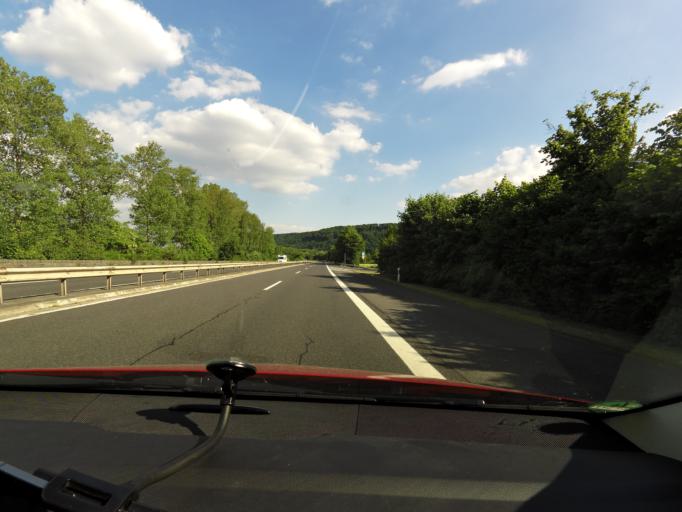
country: DE
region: Rheinland-Pfalz
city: Leutesdorf
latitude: 50.4570
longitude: 7.3642
